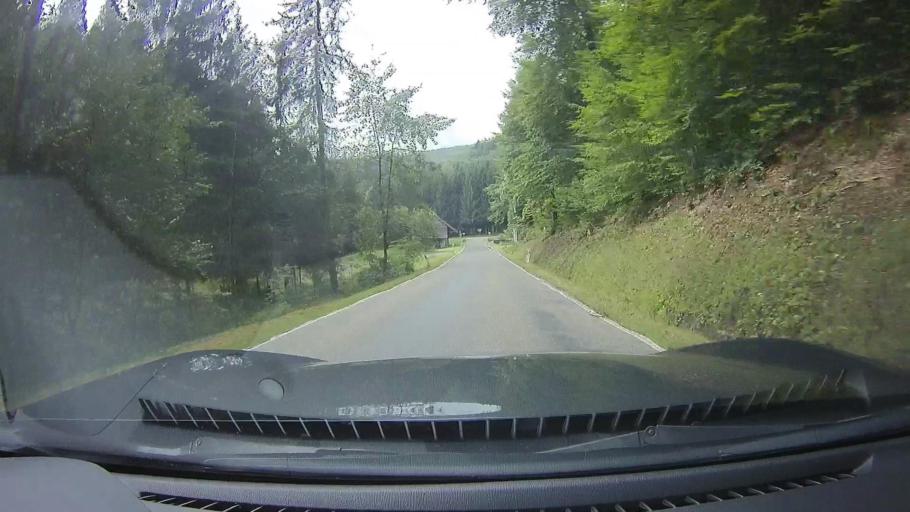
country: DE
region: Baden-Wuerttemberg
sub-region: Regierungsbezirk Stuttgart
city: Lowenstein
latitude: 49.0725
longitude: 9.4255
